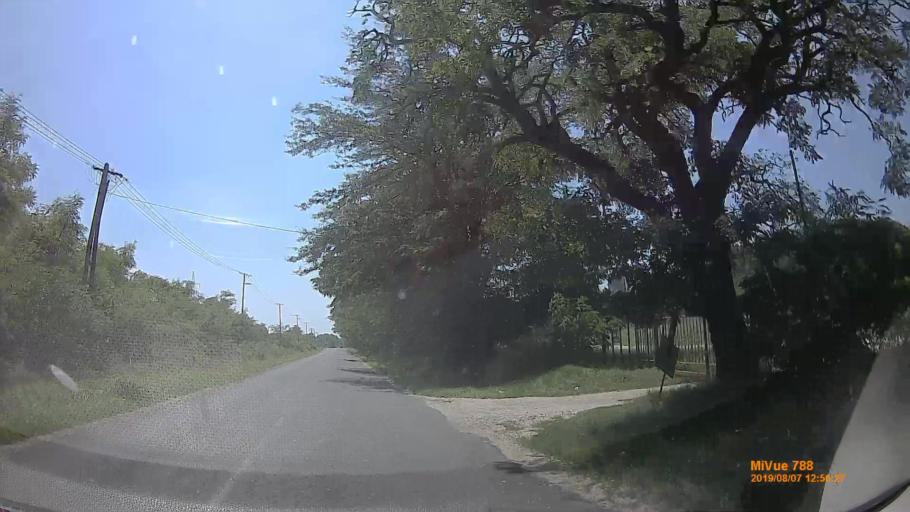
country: HU
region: Zala
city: Gyenesdias
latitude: 46.7976
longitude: 17.2676
